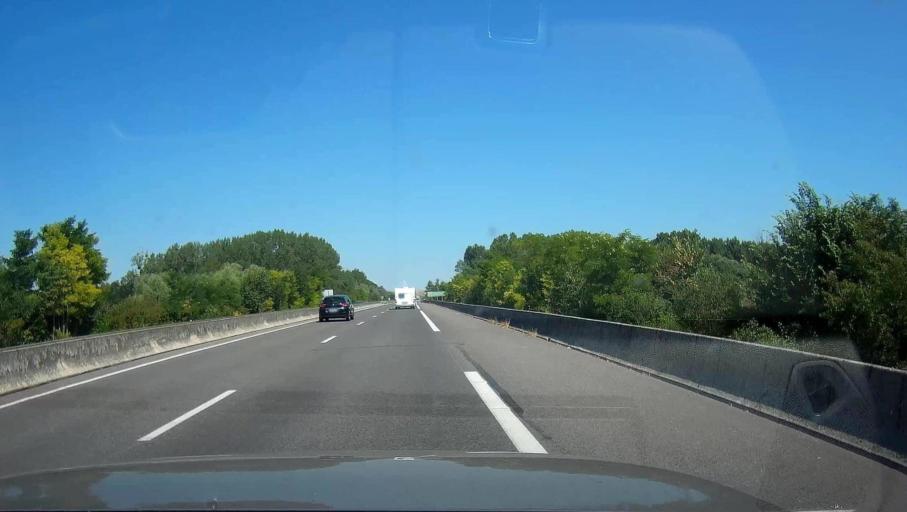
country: FR
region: Champagne-Ardenne
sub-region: Departement de l'Aube
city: Arcis-sur-Aube
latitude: 48.5364
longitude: 4.1846
